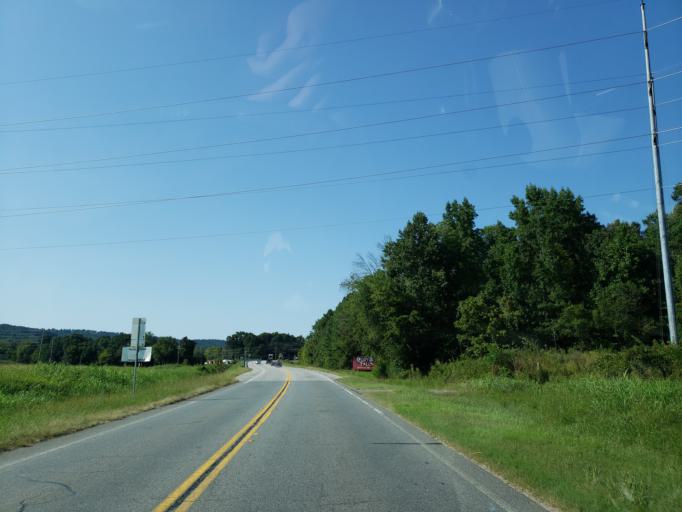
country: US
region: Georgia
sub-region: Catoosa County
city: Ringgold
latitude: 34.9021
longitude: -85.0759
